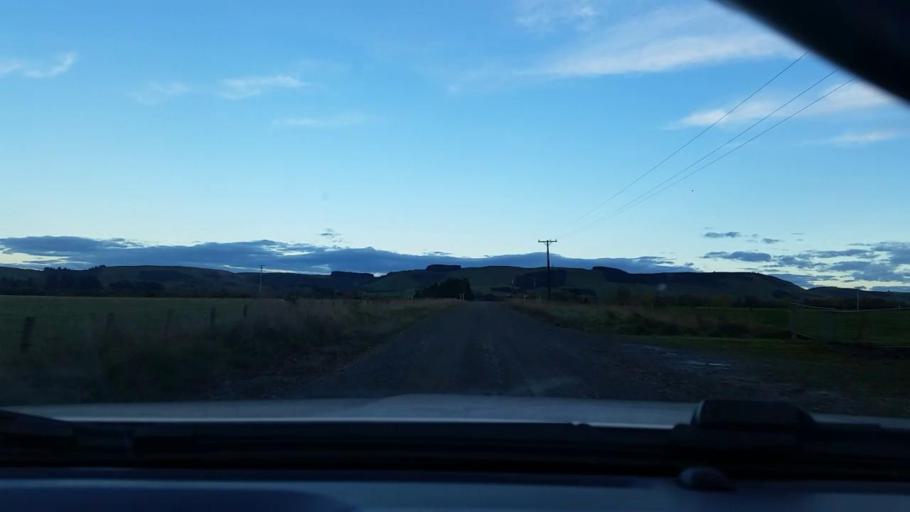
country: NZ
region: Southland
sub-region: Southland District
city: Winton
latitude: -46.1092
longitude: 168.4391
